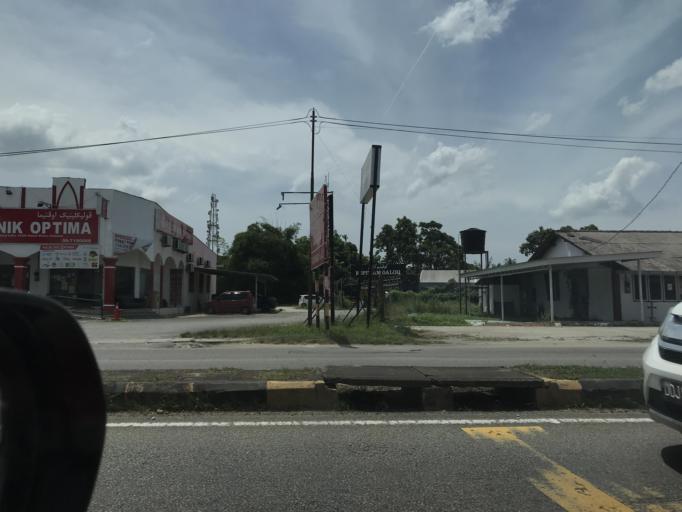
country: MY
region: Kelantan
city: Kota Bharu
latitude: 6.1199
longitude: 102.2105
